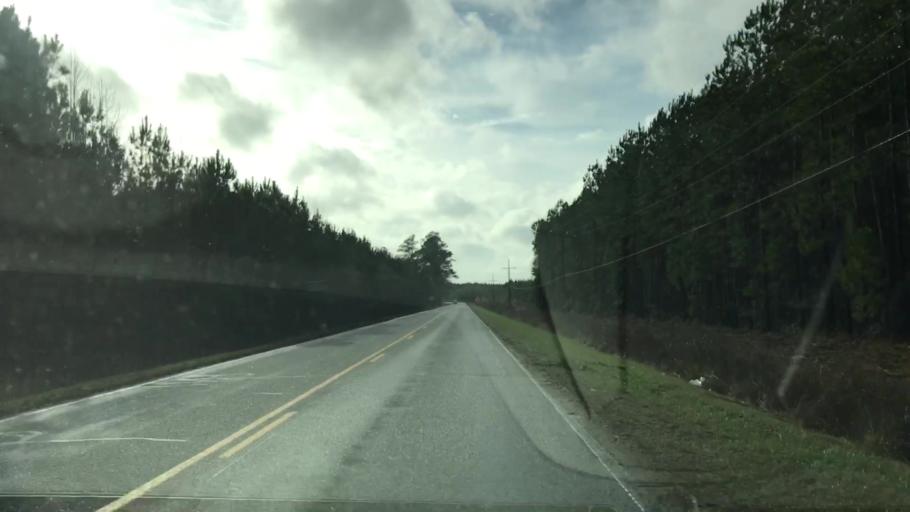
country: US
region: South Carolina
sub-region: Williamsburg County
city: Andrews
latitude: 33.4214
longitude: -79.5964
